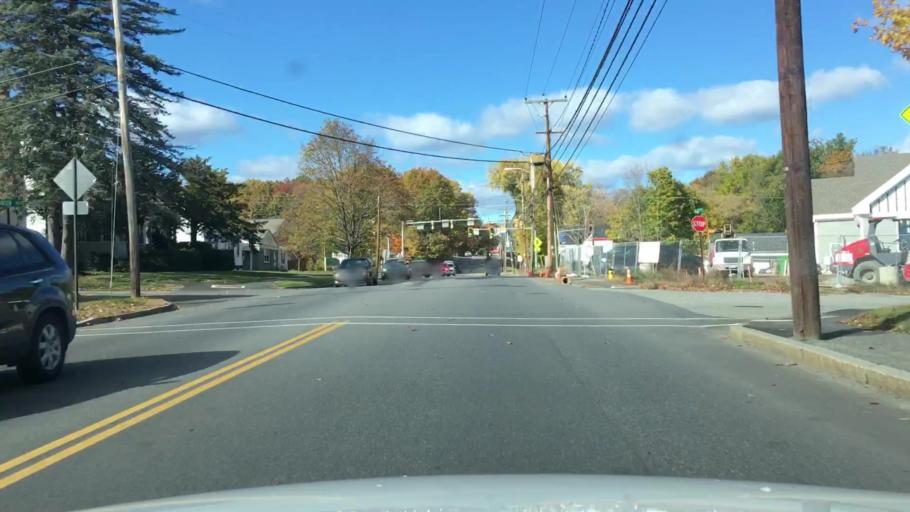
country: US
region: Maine
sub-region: Kennebec County
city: Waterville
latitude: 44.5615
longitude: -69.6348
